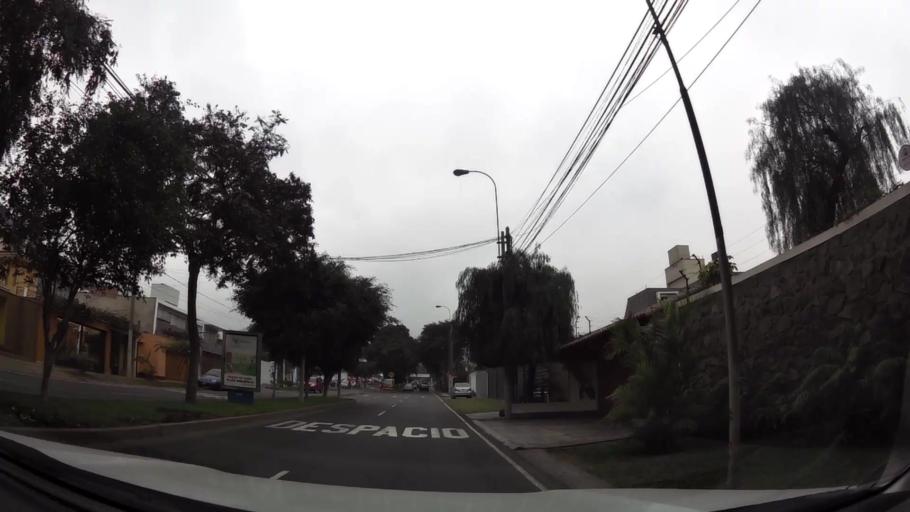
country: PE
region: Lima
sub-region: Lima
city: La Molina
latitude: -12.0783
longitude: -76.9191
